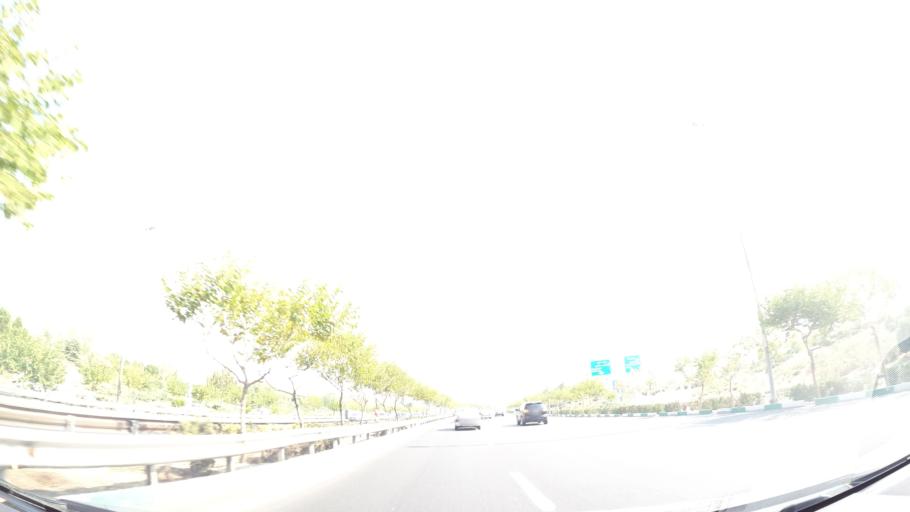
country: IR
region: Tehran
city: Shahr-e Qods
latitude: 35.7597
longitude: 51.2557
